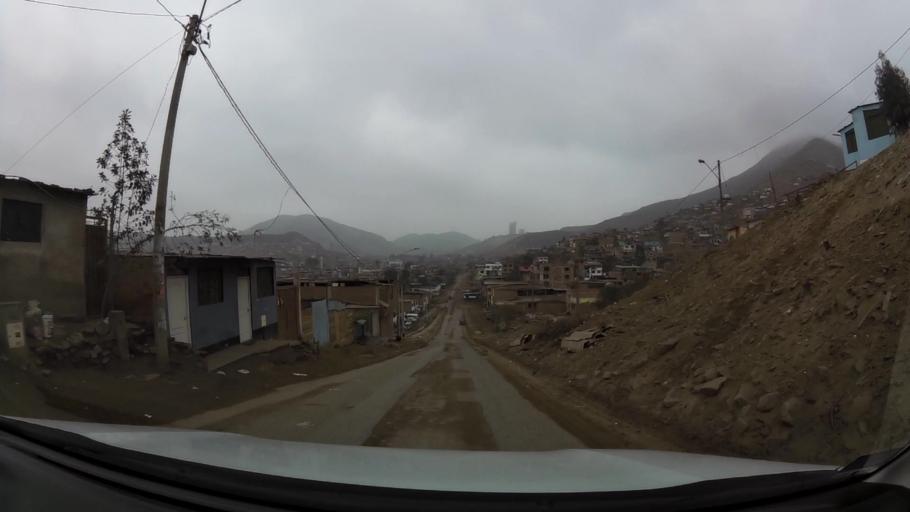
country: PE
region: Lima
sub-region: Lima
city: Cieneguilla
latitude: -12.2142
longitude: -76.9024
